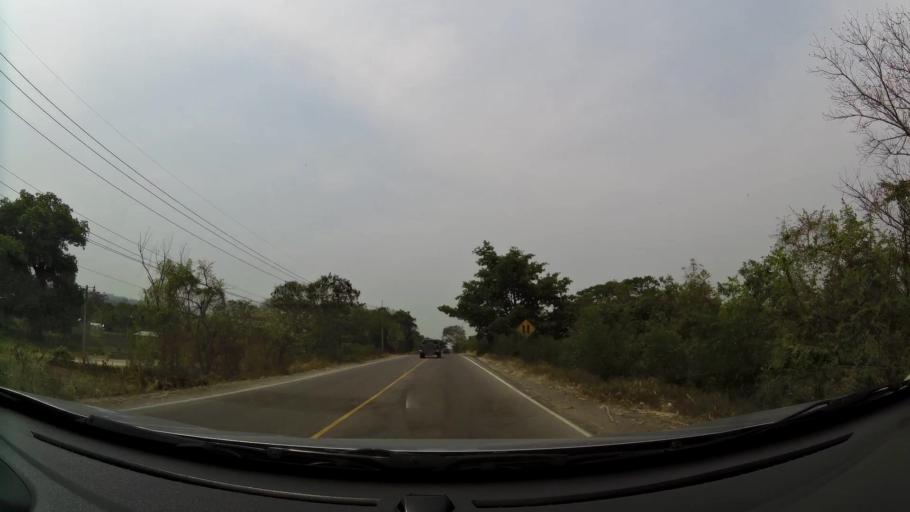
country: HN
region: Cortes
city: Potrerillos
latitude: 15.1852
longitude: -87.9618
